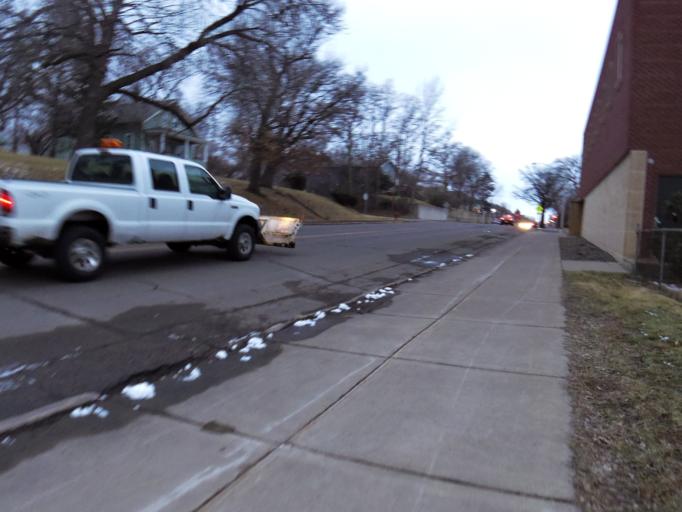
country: US
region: Wisconsin
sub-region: Saint Croix County
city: Hudson
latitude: 44.9786
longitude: -92.7572
